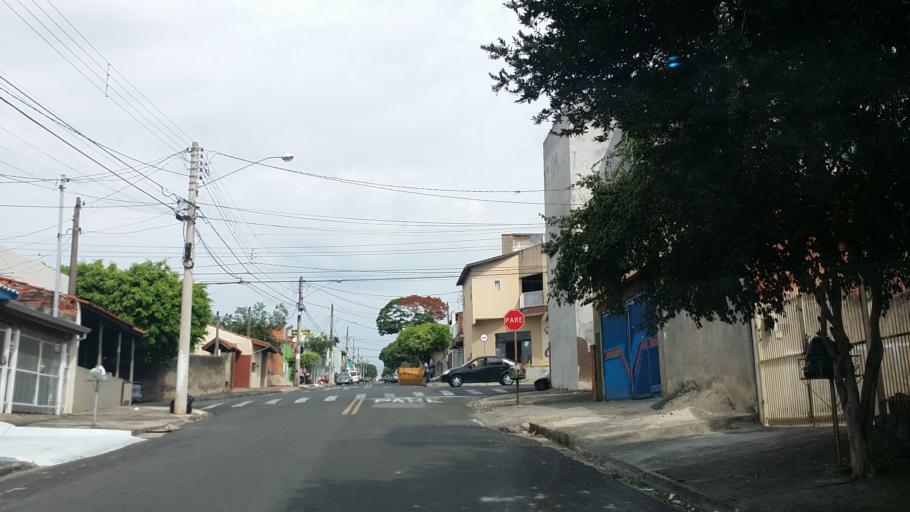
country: BR
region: Sao Paulo
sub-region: Indaiatuba
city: Indaiatuba
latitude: -23.1205
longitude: -47.2362
